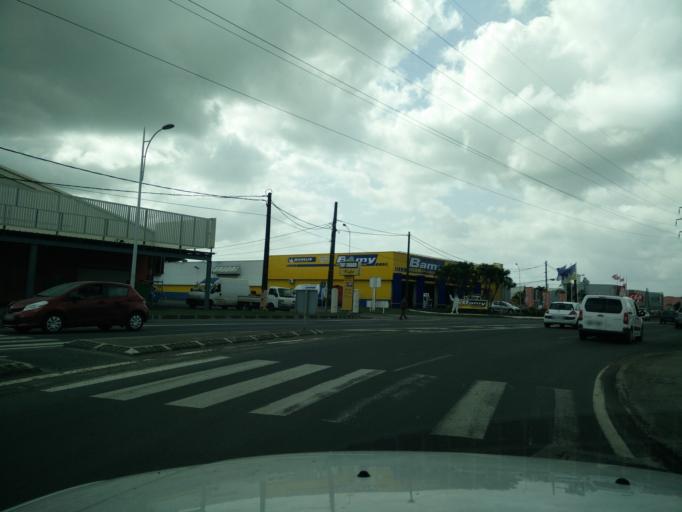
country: GP
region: Guadeloupe
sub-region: Guadeloupe
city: Pointe-a-Pitre
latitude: 16.2432
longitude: -61.5549
